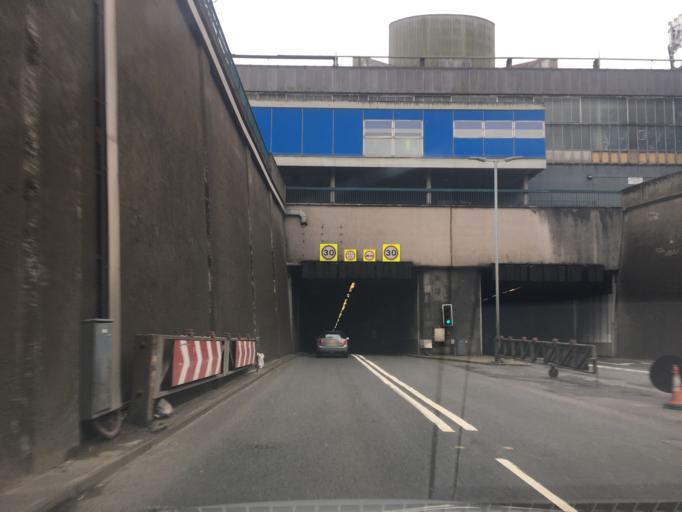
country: GB
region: Scotland
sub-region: East Dunbartonshire
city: Bearsden
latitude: 55.8722
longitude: -4.3296
